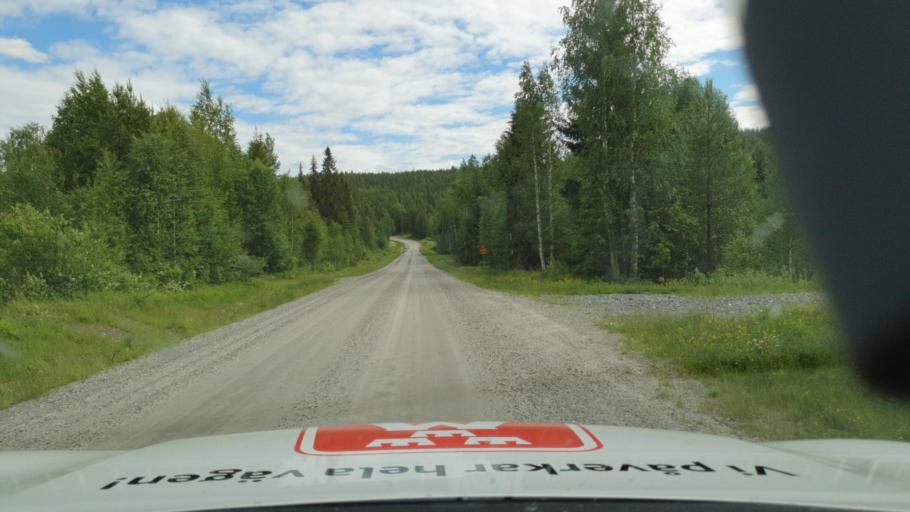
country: SE
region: Vaesterbotten
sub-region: Norsjo Kommun
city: Norsjoe
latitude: 64.8348
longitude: 19.5370
